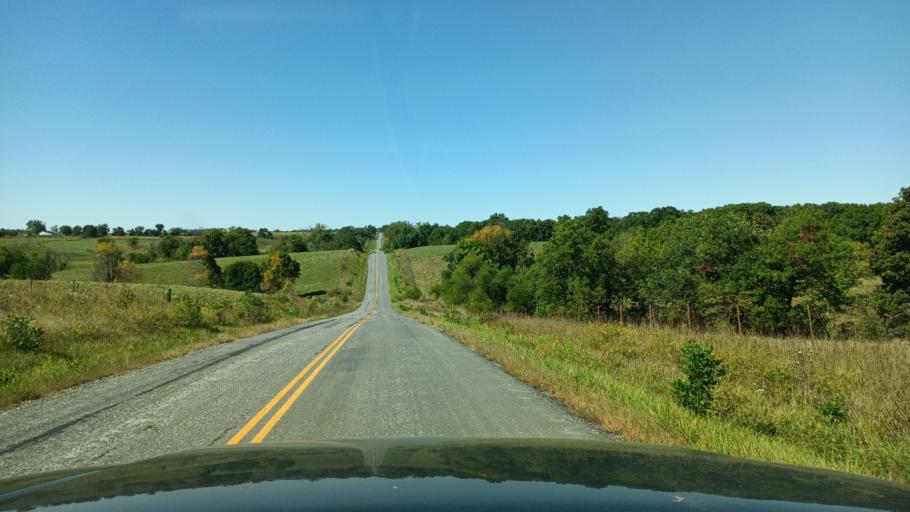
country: US
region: Missouri
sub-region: Adair County
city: Kirksville
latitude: 40.3301
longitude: -92.5439
